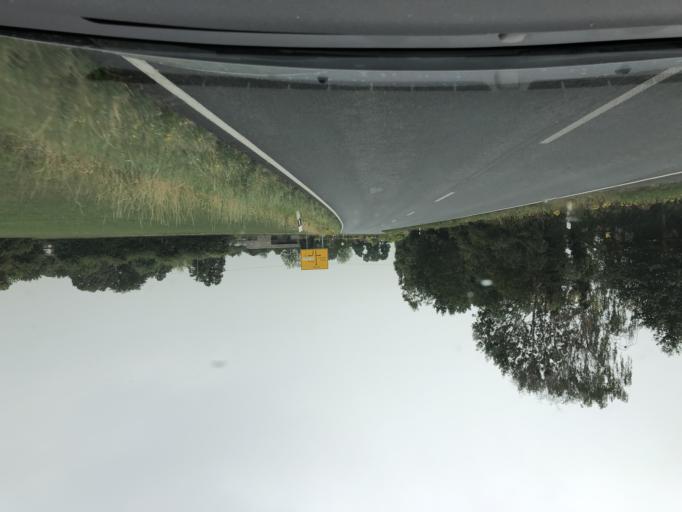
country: DE
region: North Rhine-Westphalia
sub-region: Regierungsbezirk Munster
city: Sudlohn
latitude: 51.9226
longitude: 6.8467
